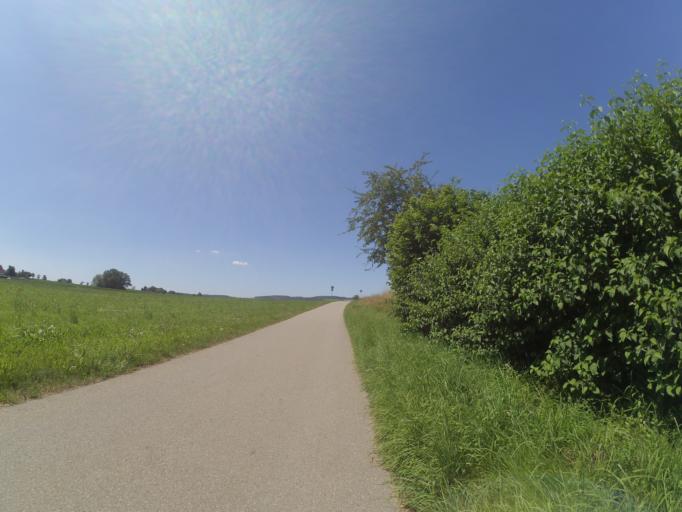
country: DE
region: Baden-Wuerttemberg
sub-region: Tuebingen Region
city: Aulendorf
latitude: 47.9334
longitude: 9.6643
